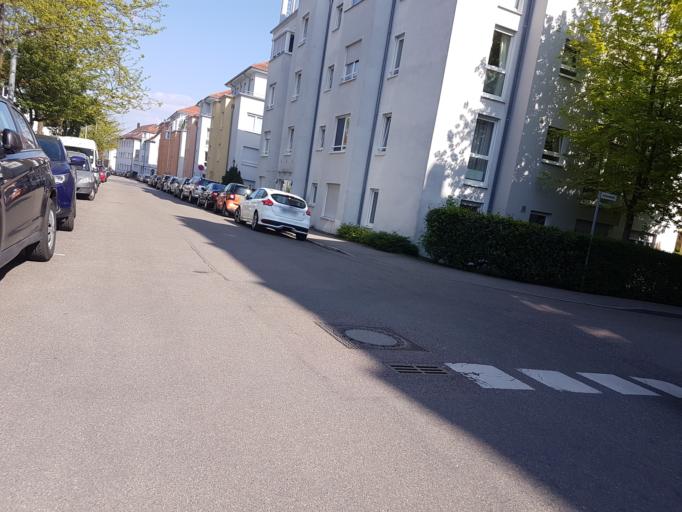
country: DE
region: Baden-Wuerttemberg
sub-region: Regierungsbezirk Stuttgart
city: Ludwigsburg
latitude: 48.8952
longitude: 9.1742
